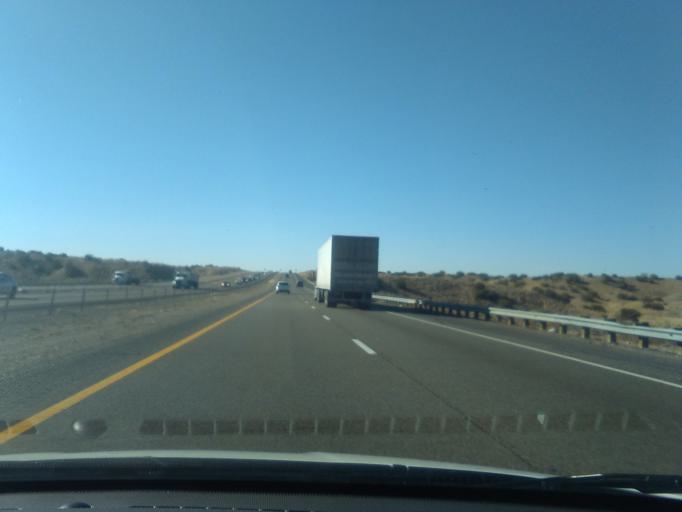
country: US
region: New Mexico
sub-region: Sandoval County
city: San Felipe Pueblo
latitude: 35.3652
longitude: -106.4861
